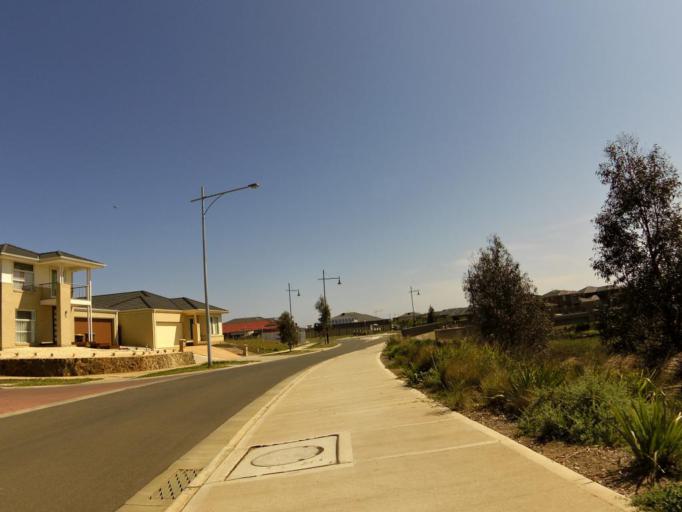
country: AU
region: Victoria
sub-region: Wyndham
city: Hoppers Crossing
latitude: -37.8799
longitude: 144.7243
